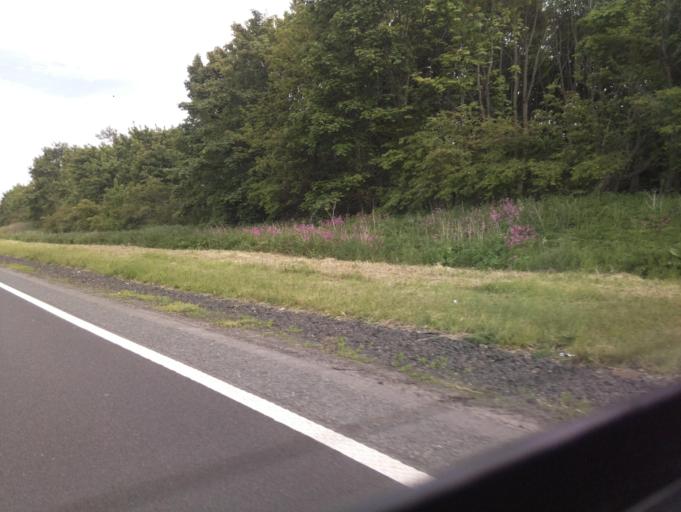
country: GB
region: Scotland
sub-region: The Scottish Borders
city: Eyemouth
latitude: 55.8487
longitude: -2.1208
